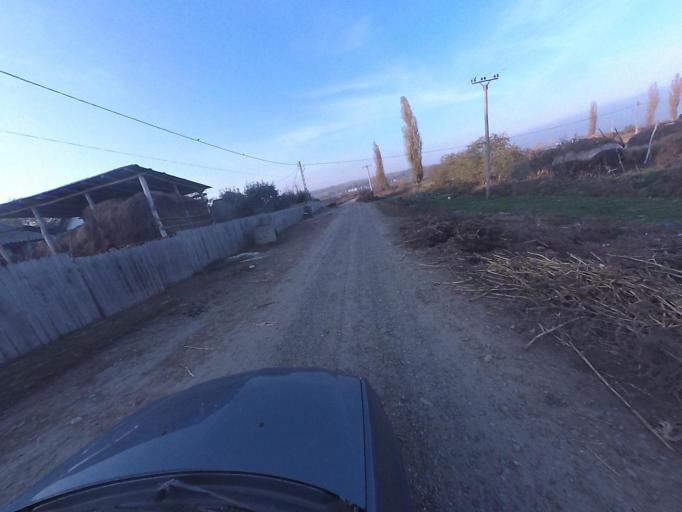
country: RO
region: Vaslui
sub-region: Comuna Bacesti
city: Bacesti
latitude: 46.8094
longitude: 27.2365
